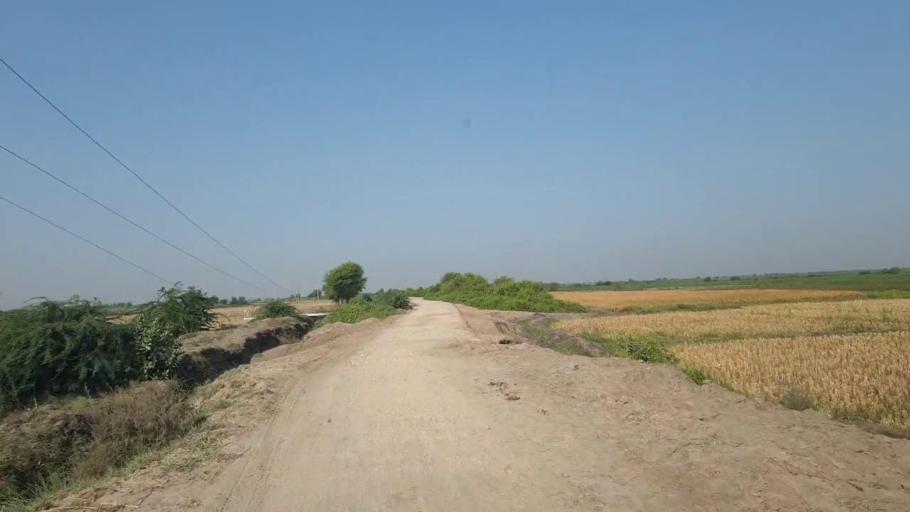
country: PK
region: Sindh
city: Badin
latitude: 24.5181
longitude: 68.7808
